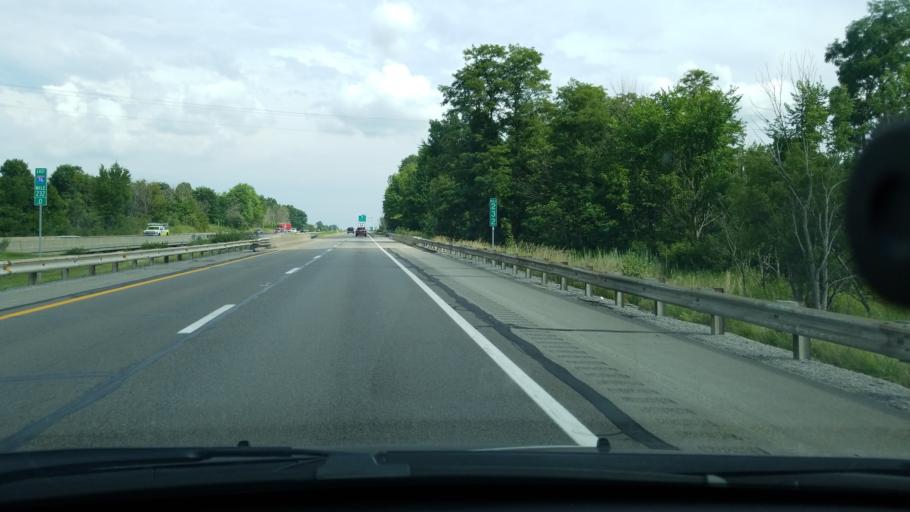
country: US
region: Ohio
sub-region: Mahoning County
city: Boardman
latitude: 40.9754
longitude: -80.6702
